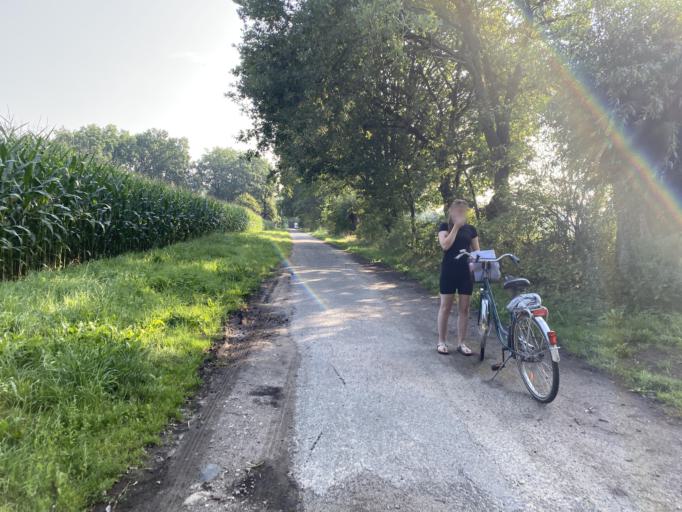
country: DE
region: Lower Saxony
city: Dahlenburg
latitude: 53.1746
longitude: 10.6878
